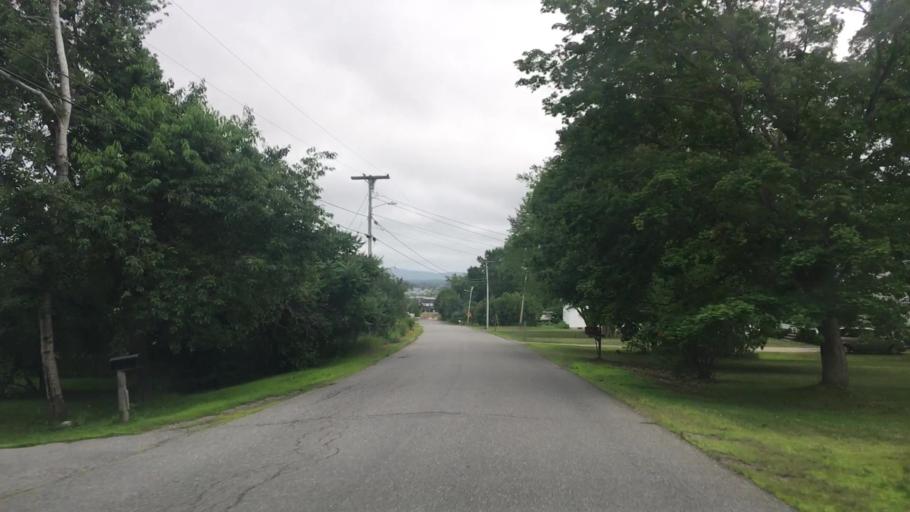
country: US
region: Maine
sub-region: Penobscot County
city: Veazie
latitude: 44.8452
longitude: -68.7464
